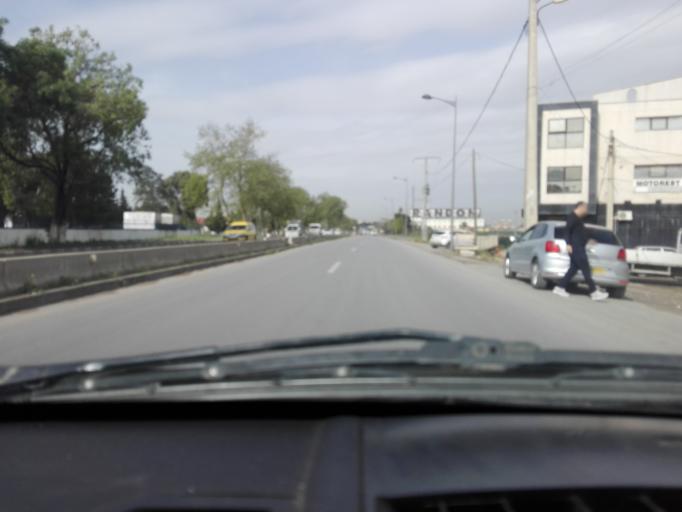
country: DZ
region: Alger
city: Dar el Beida
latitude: 36.7268
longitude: 3.2066
